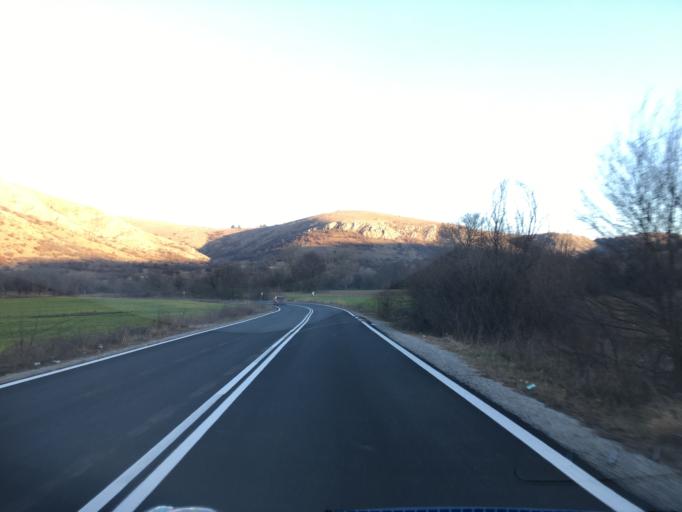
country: GR
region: West Macedonia
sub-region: Nomos Kozanis
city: Kozani
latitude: 40.3156
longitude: 21.7577
